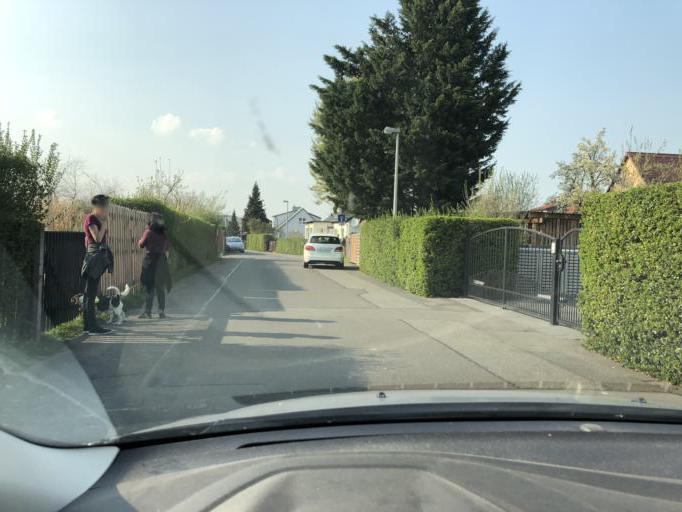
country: DE
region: Saxony
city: Rackwitz
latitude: 51.4042
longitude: 12.4120
